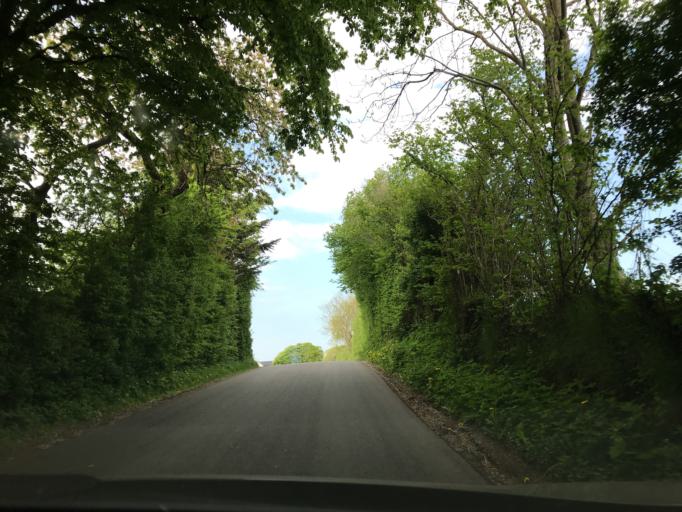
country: DK
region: South Denmark
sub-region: Middelfart Kommune
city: Norre Aby
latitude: 55.3818
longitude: 9.8493
